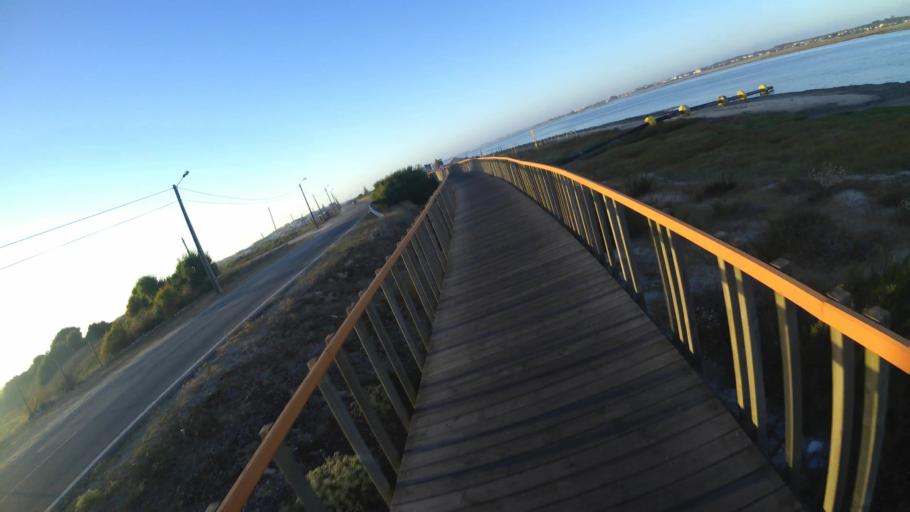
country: PT
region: Aveiro
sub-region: Ilhavo
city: Gafanha da Encarnacao
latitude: 40.6025
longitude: -8.7486
